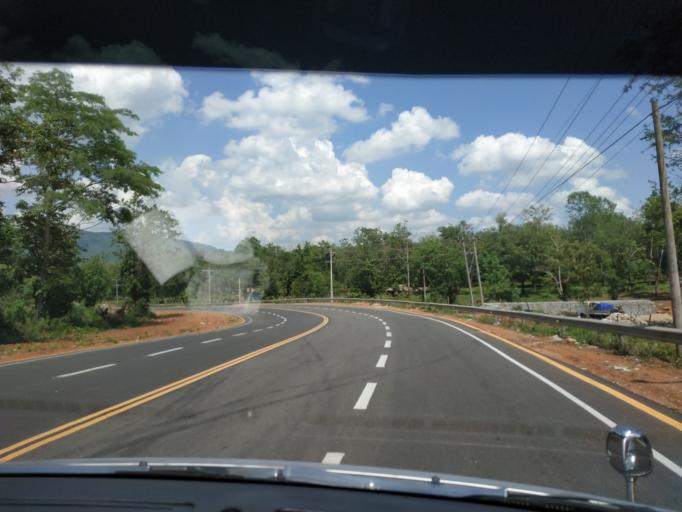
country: MM
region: Mon
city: Kyaikto
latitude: 17.3897
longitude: 97.0682
